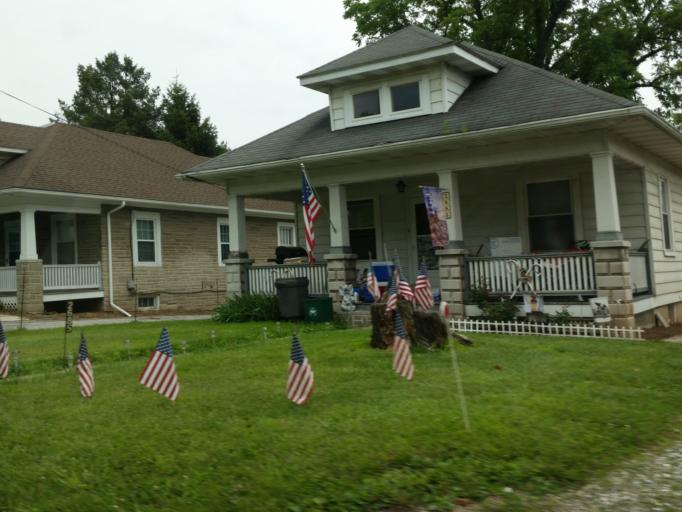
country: US
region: Pennsylvania
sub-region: York County
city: Emigsville
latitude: 40.0065
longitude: -76.7496
